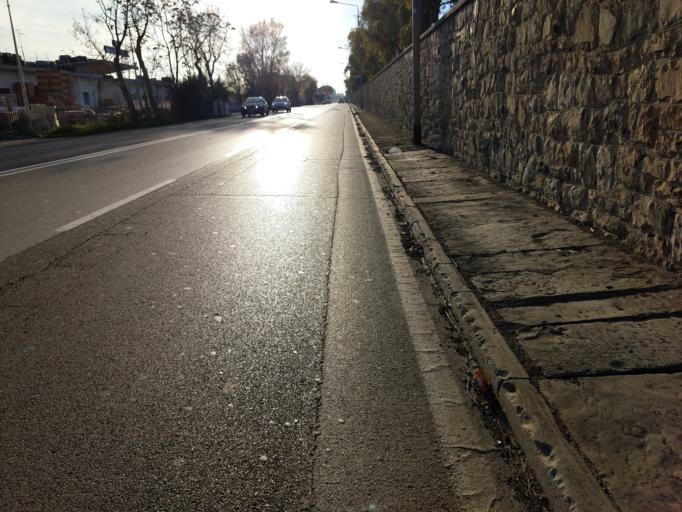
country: IT
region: Apulia
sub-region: Provincia di Bari
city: Bari
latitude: 41.1138
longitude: 16.8322
